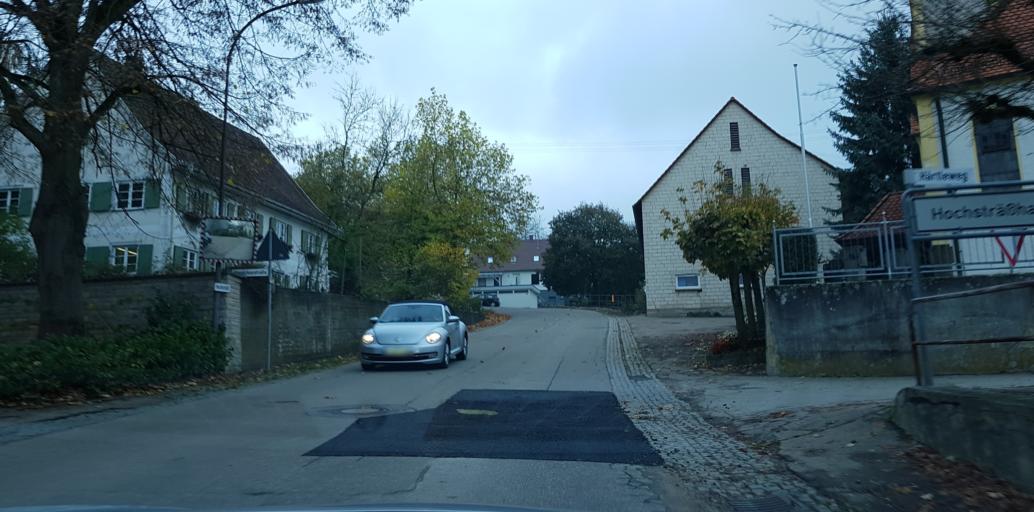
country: DE
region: Baden-Wuerttemberg
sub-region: Tuebingen Region
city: Altheim
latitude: 48.3167
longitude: 9.7773
